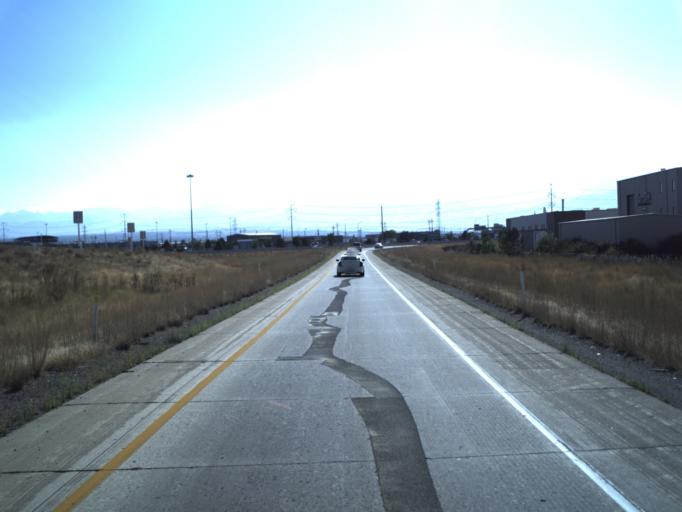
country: US
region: Utah
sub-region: Salt Lake County
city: West Valley City
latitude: 40.7277
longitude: -111.9521
